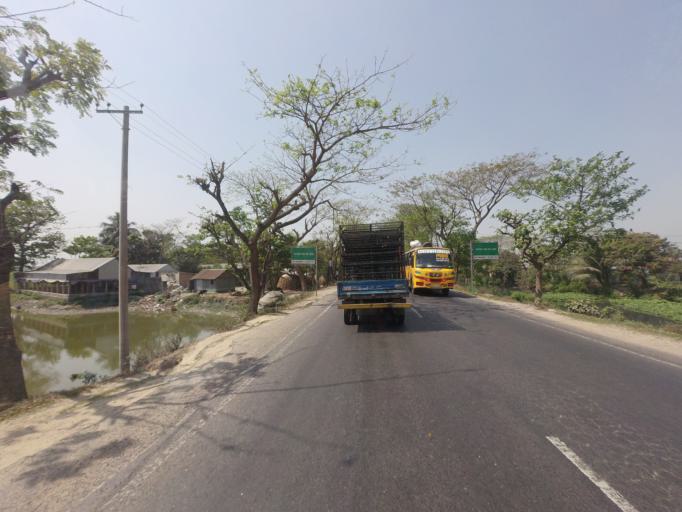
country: BD
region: Dhaka
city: Bhairab Bazar
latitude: 24.0453
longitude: 91.0720
